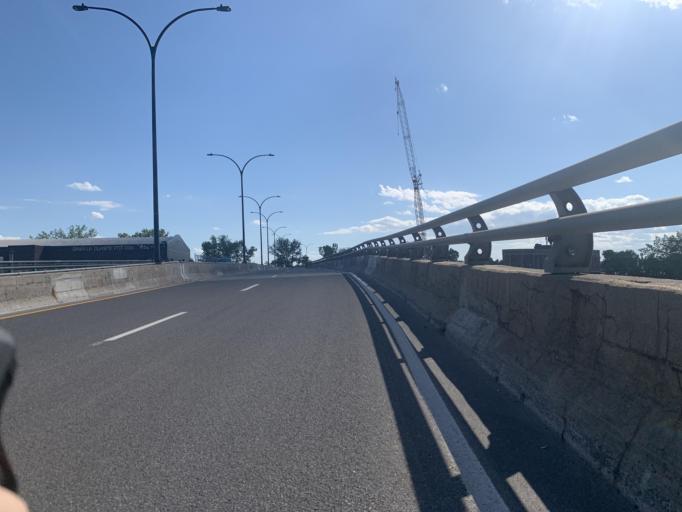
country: CA
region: Quebec
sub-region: Montreal
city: Montreal
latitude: 45.5300
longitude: -73.6001
